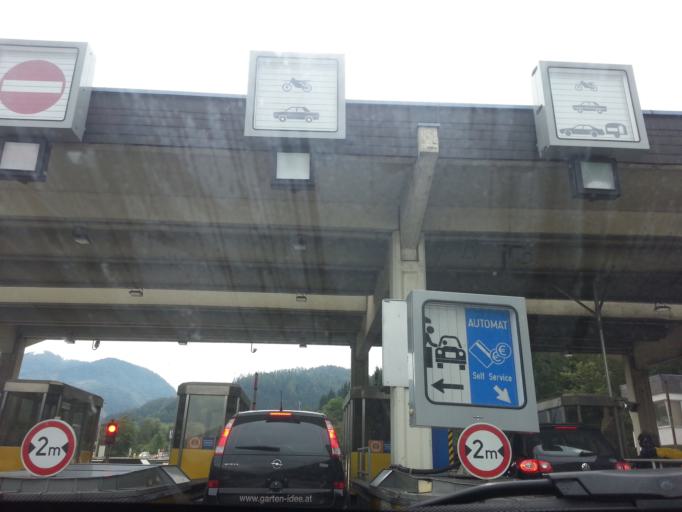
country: AT
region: Styria
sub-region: Politischer Bezirk Leoben
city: Sankt Michael in Obersteiermark
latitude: 47.3234
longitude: 15.0298
